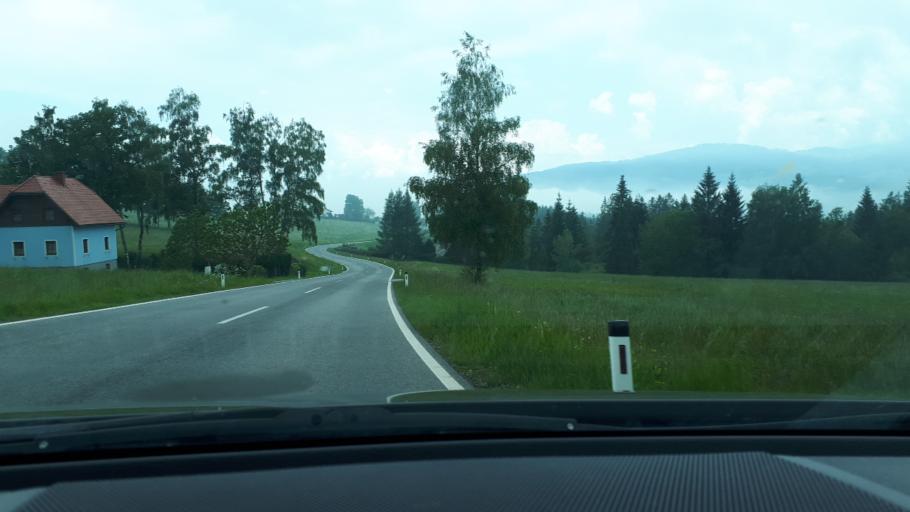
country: AT
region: Carinthia
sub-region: Politischer Bezirk Wolfsberg
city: Preitenegg
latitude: 46.9315
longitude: 14.9515
